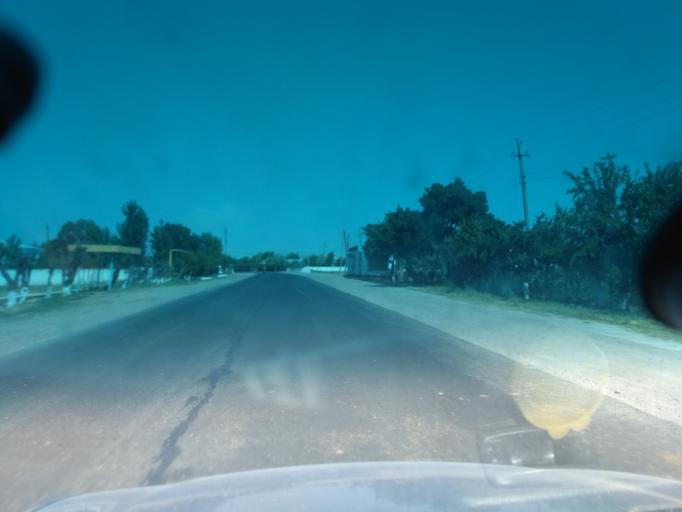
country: UZ
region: Sirdaryo
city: Guliston
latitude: 40.4863
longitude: 68.8984
